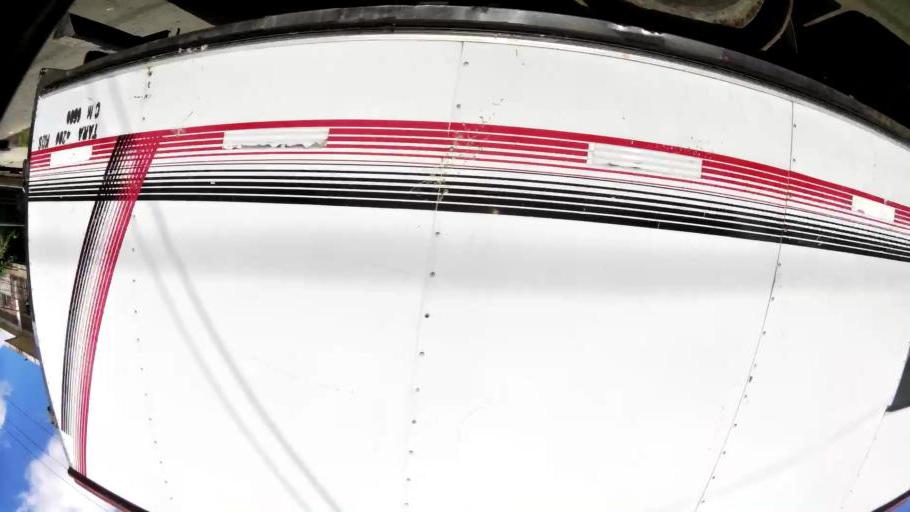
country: AR
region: Buenos Aires
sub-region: Partido de Lanus
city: Lanus
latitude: -34.6774
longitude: -58.4299
